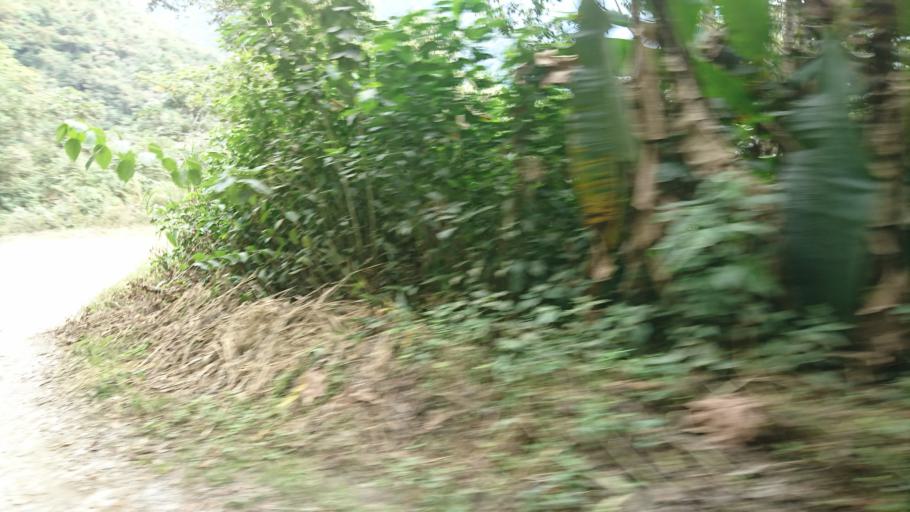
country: BO
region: La Paz
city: Coroico
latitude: -16.1144
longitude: -67.7828
